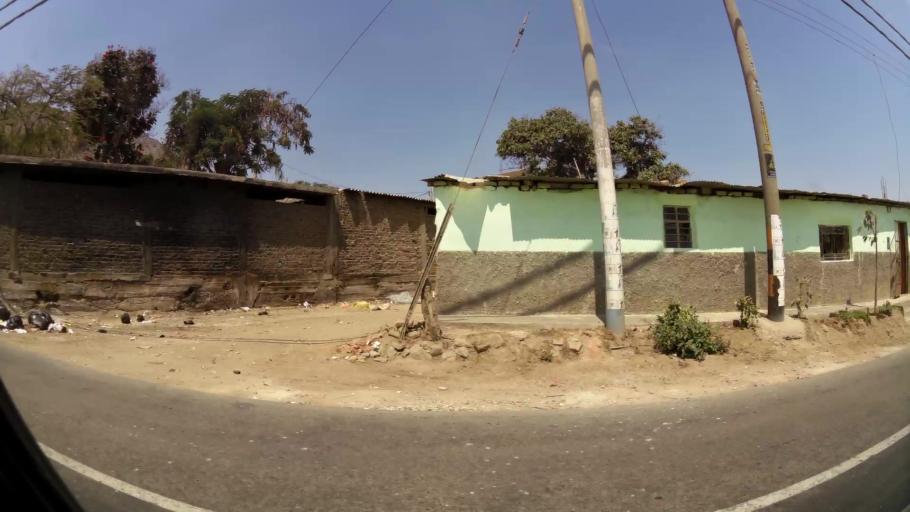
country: PE
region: La Libertad
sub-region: Chepen
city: Chepen
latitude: -7.2188
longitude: -79.4324
